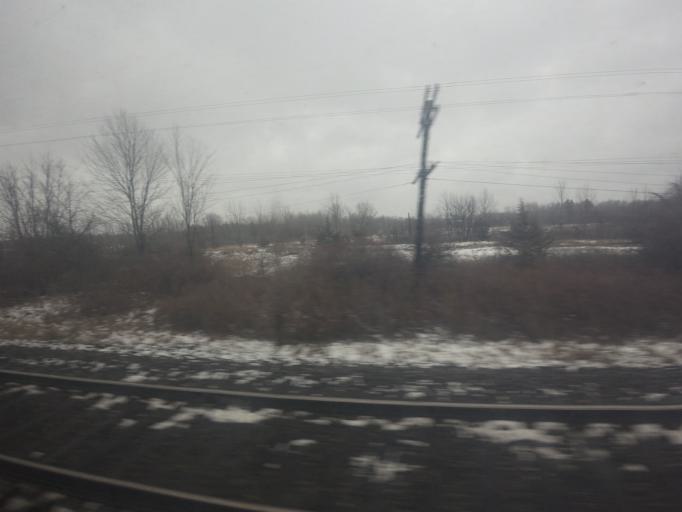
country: CA
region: Ontario
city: Quinte West
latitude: 44.0740
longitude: -77.6559
